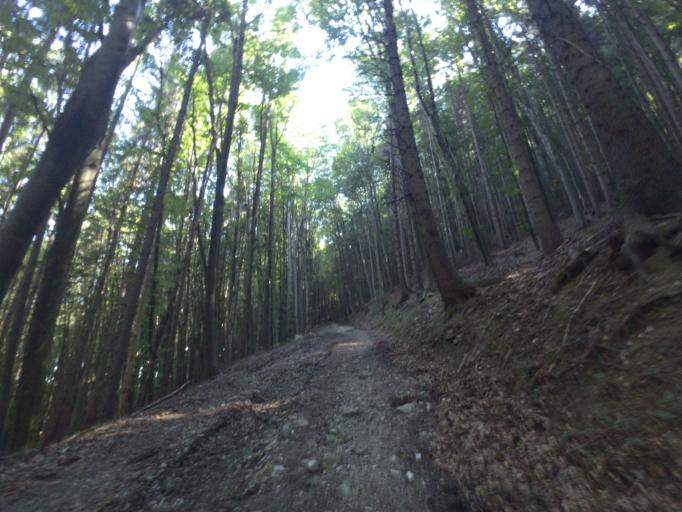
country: AT
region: Salzburg
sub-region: Politischer Bezirk Salzburg-Umgebung
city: Mattsee
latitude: 47.9518
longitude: 13.1054
